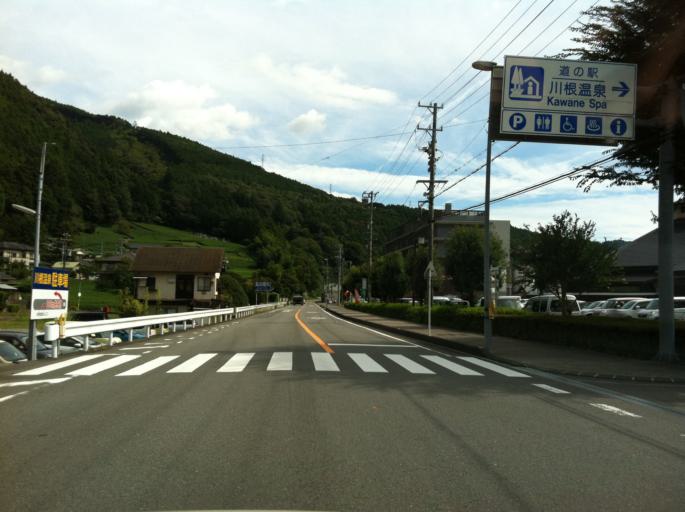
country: JP
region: Shizuoka
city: Kanaya
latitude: 34.9601
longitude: 138.0900
